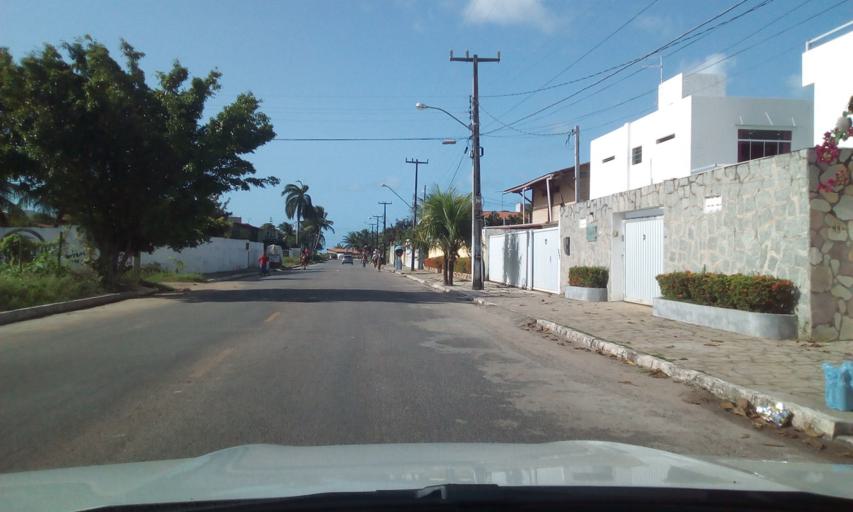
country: BR
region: Paraiba
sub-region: Joao Pessoa
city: Joao Pessoa
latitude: -7.1573
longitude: -34.7942
